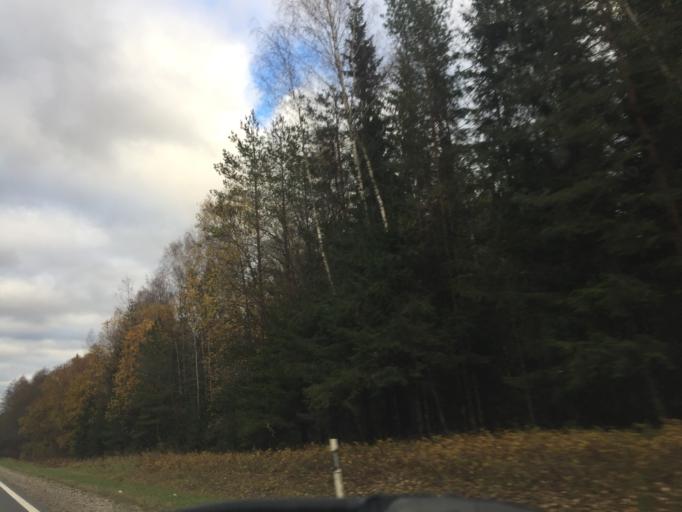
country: LV
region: Skrunda
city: Skrunda
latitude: 56.6559
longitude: 21.9325
